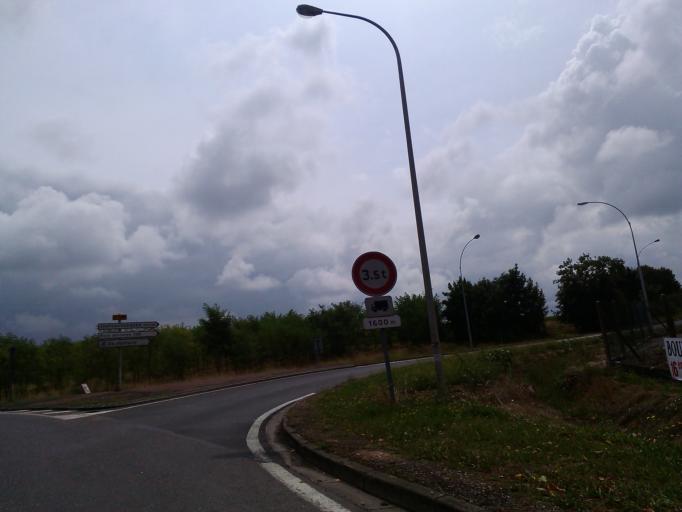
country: FR
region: Poitou-Charentes
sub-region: Departement de la Charente
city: Saint-Brice
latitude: 45.6812
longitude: -0.2931
